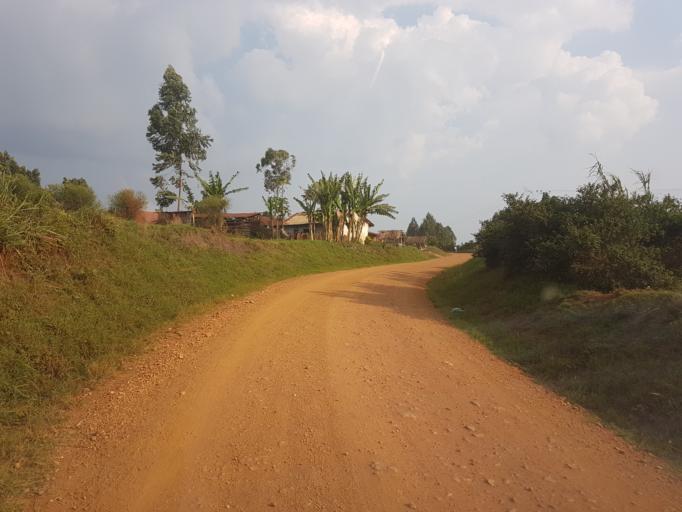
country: UG
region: Western Region
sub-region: Rukungiri District
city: Rukungiri
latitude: -0.6545
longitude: 29.8616
